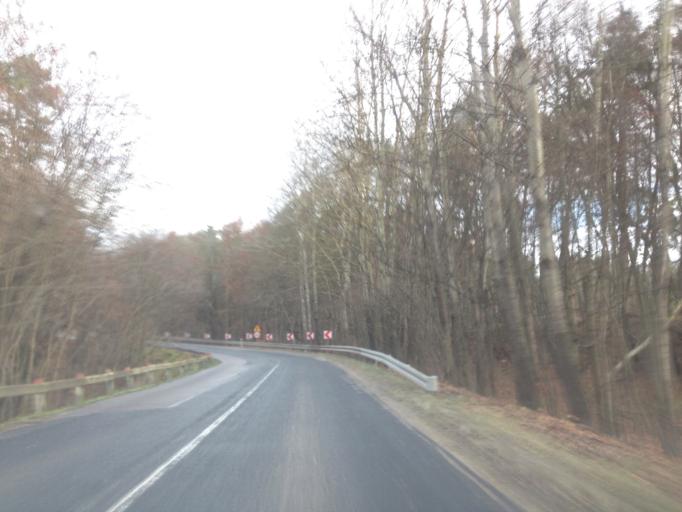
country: PL
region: Pomeranian Voivodeship
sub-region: Powiat gdanski
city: Kolbudy
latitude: 54.2643
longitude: 18.4289
